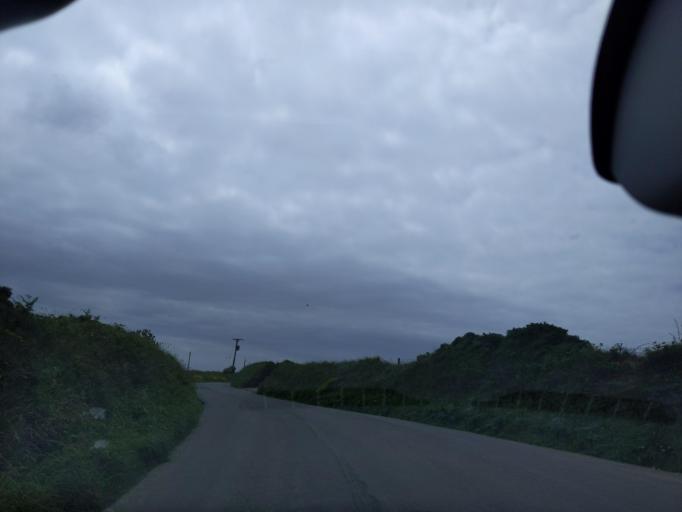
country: IM
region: Douglas
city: Douglas
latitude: 54.1497
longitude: -4.5616
